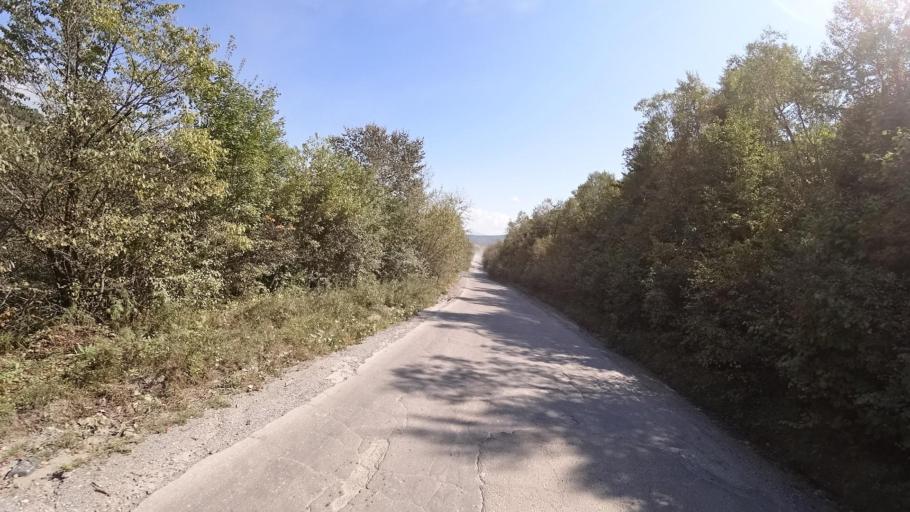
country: RU
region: Jewish Autonomous Oblast
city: Londoko
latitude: 49.0075
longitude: 131.9076
